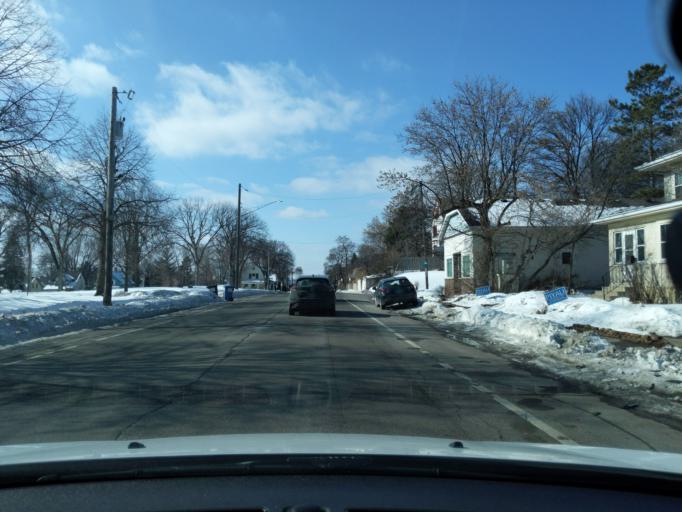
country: US
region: Minnesota
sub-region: Hennepin County
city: Saint Anthony
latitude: 45.0133
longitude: -93.2352
